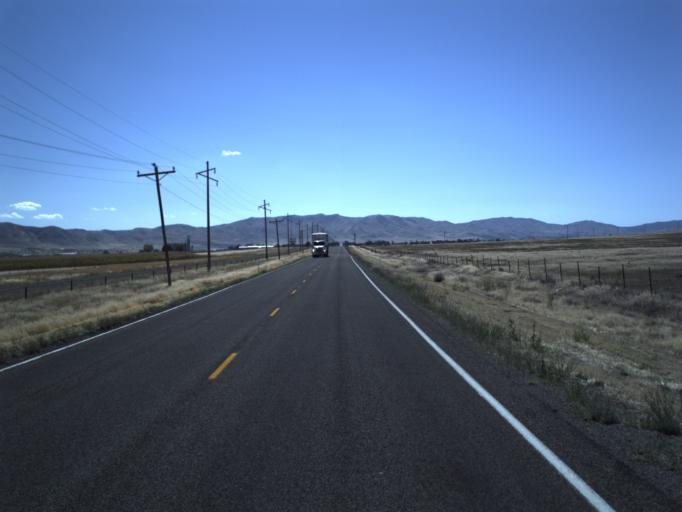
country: US
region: Utah
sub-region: Utah County
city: Genola
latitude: 39.9880
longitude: -111.9574
